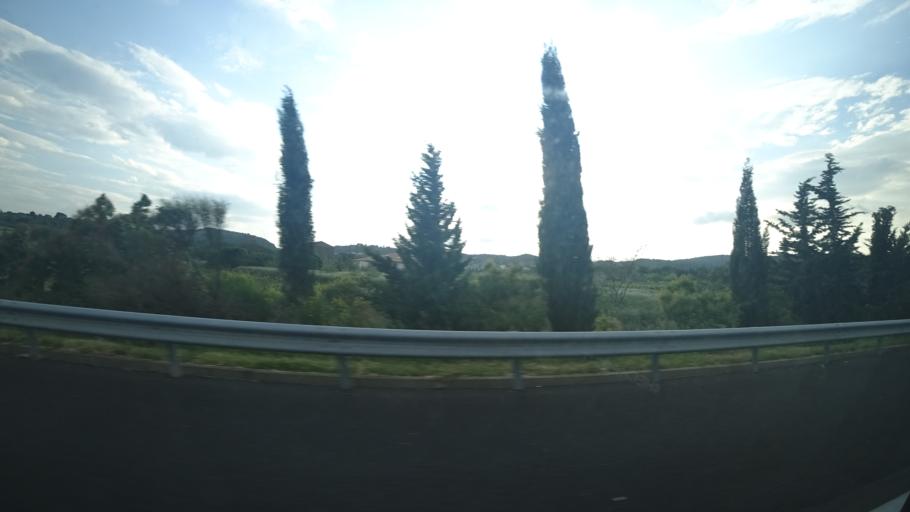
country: FR
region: Languedoc-Roussillon
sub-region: Departement de l'Herault
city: Nebian
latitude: 43.6338
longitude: 3.4476
